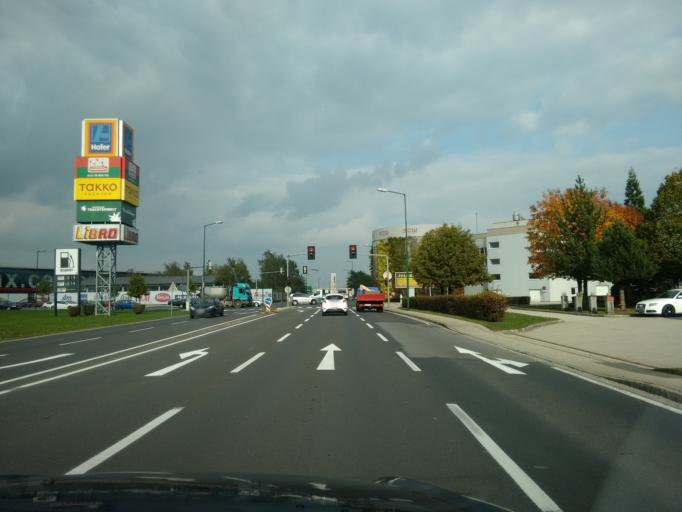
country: AT
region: Upper Austria
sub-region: Wels-Land
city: Gunskirchen
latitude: 48.1431
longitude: 13.9717
